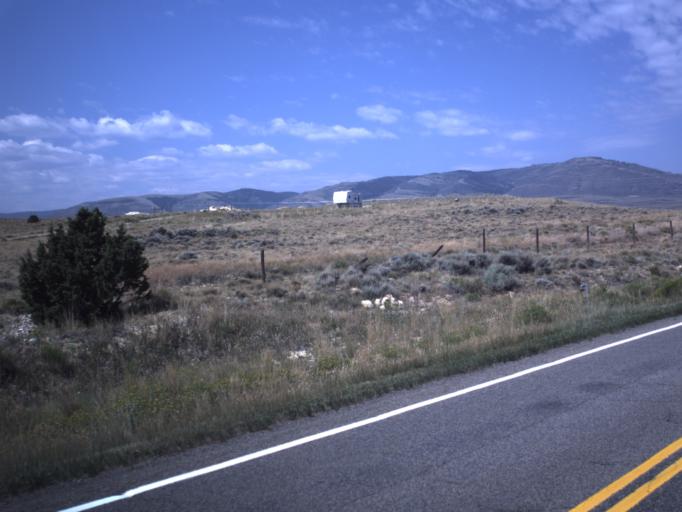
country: US
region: Utah
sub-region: Daggett County
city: Manila
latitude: 40.9793
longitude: -109.8059
